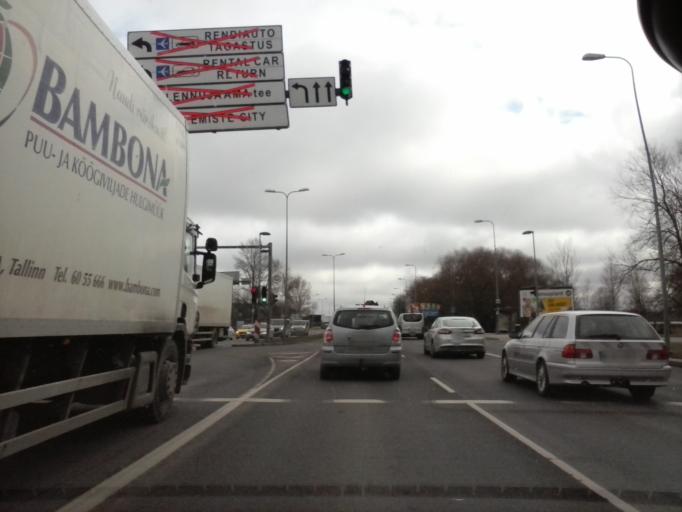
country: EE
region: Harju
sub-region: Tallinna linn
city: Tallinn
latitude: 59.4201
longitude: 24.7911
